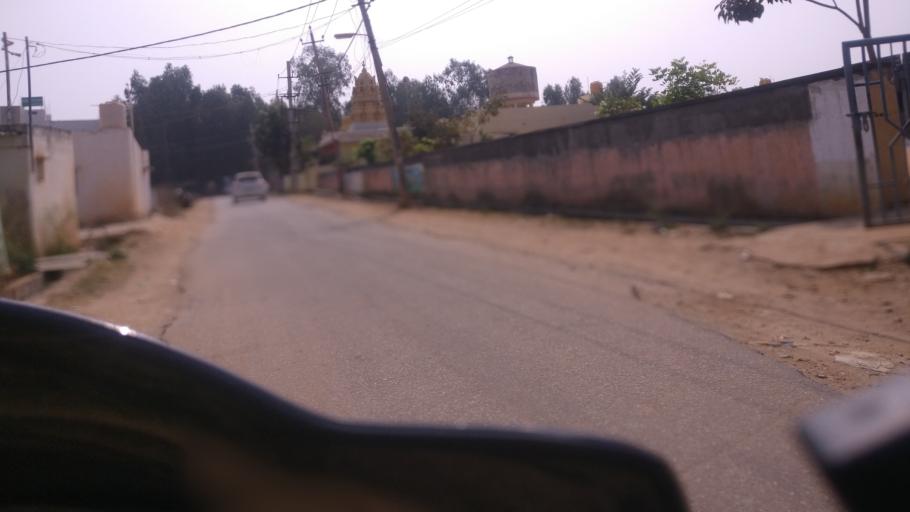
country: IN
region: Karnataka
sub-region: Bangalore Urban
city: Bangalore
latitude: 12.8975
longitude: 77.6831
